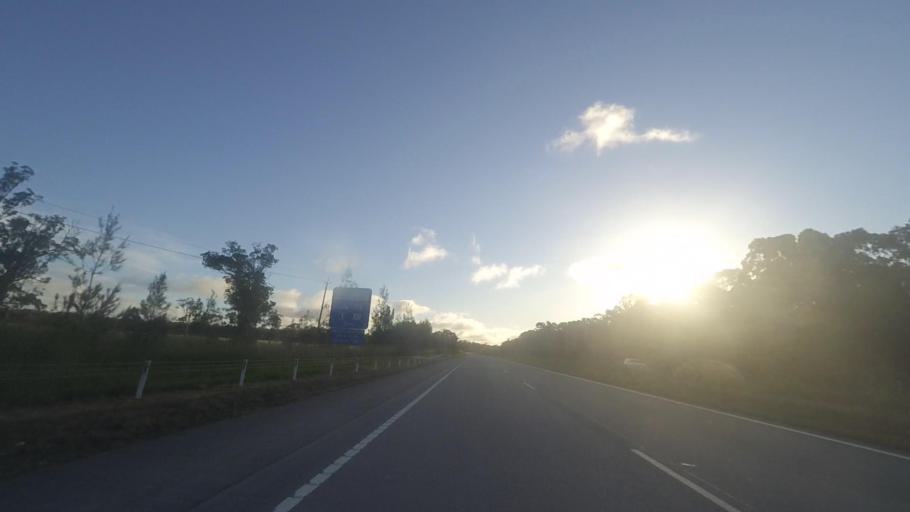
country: AU
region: New South Wales
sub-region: Great Lakes
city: Hawks Nest
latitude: -32.5412
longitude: 152.1669
